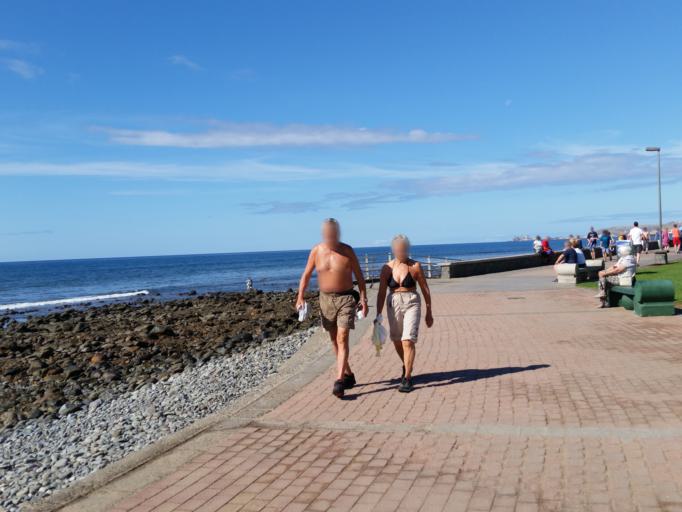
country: ES
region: Canary Islands
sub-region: Provincia de Las Palmas
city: Maspalomas
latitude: 27.7352
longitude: -15.5994
